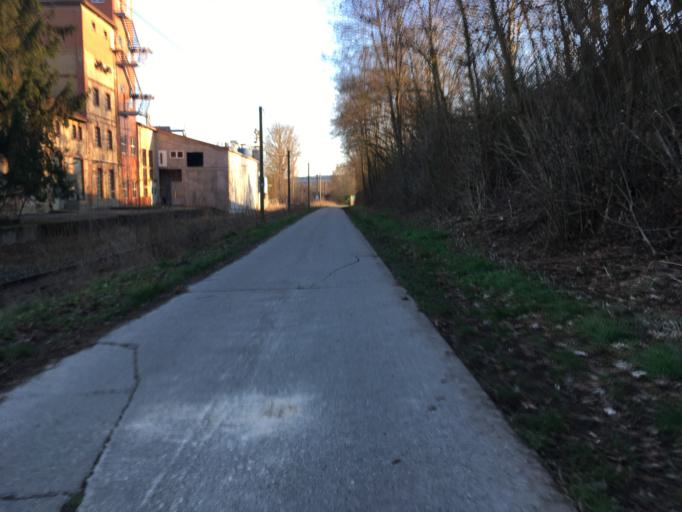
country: DE
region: Baden-Wuerttemberg
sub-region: Regierungsbezirk Stuttgart
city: Ittlingen
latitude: 49.1657
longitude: 8.9372
